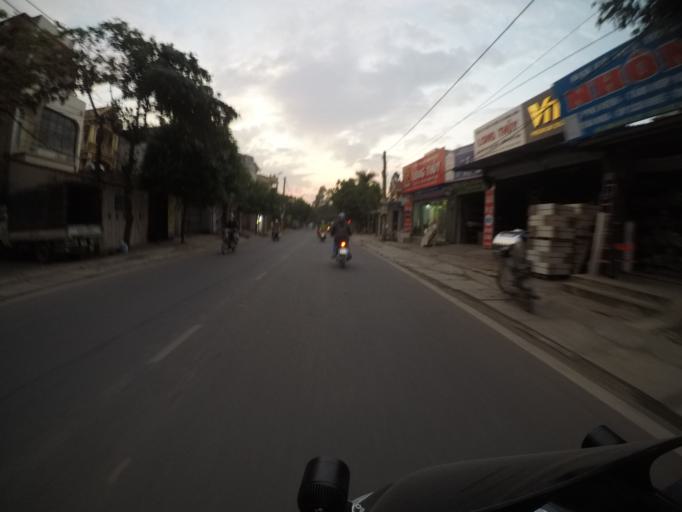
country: VN
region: Vinh Phuc
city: Phuc Yen
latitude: 21.2746
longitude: 105.7270
